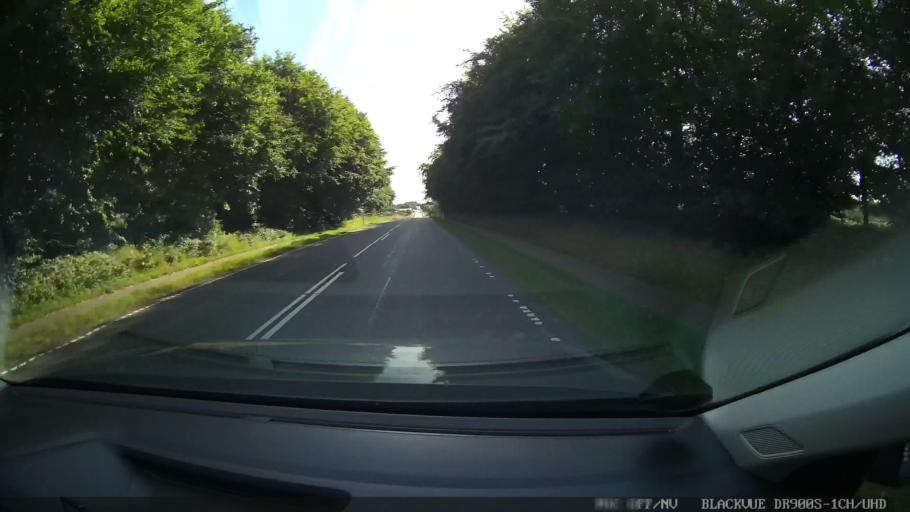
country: DK
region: North Denmark
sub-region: Mariagerfjord Kommune
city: Arden
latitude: 56.7745
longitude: 9.7999
